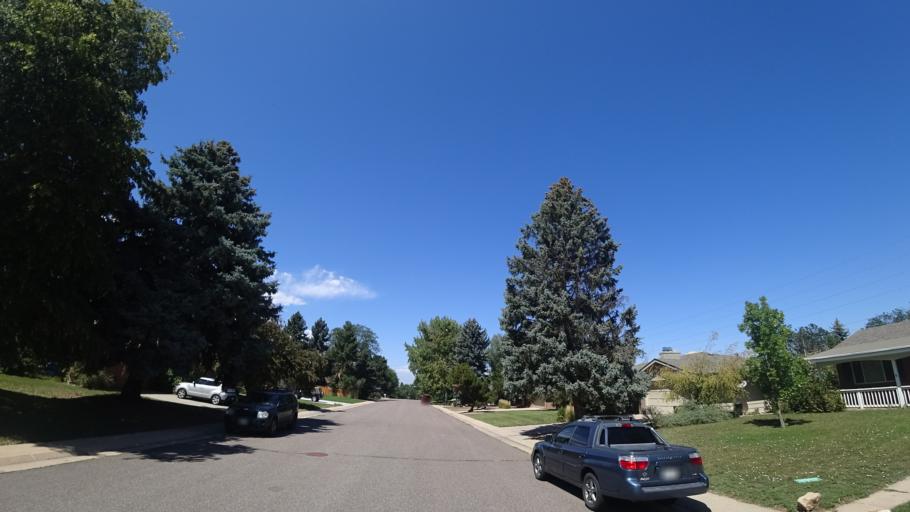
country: US
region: Colorado
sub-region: Arapahoe County
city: Greenwood Village
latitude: 39.6062
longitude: -104.9762
